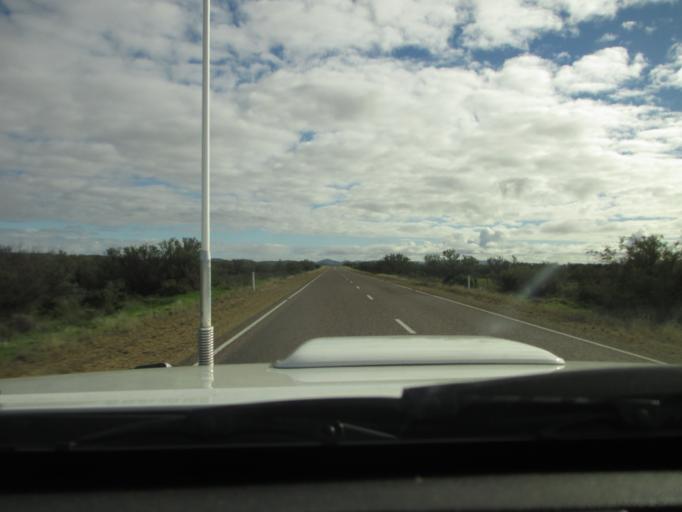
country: AU
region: South Australia
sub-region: Flinders Ranges
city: Quorn
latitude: -32.3517
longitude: 138.4891
